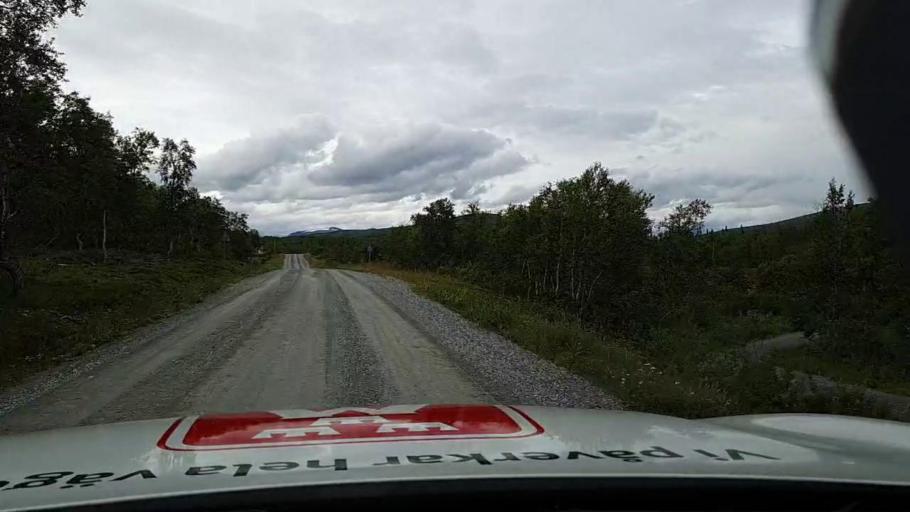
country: SE
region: Jaemtland
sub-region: Are Kommun
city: Are
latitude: 62.8803
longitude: 12.7287
